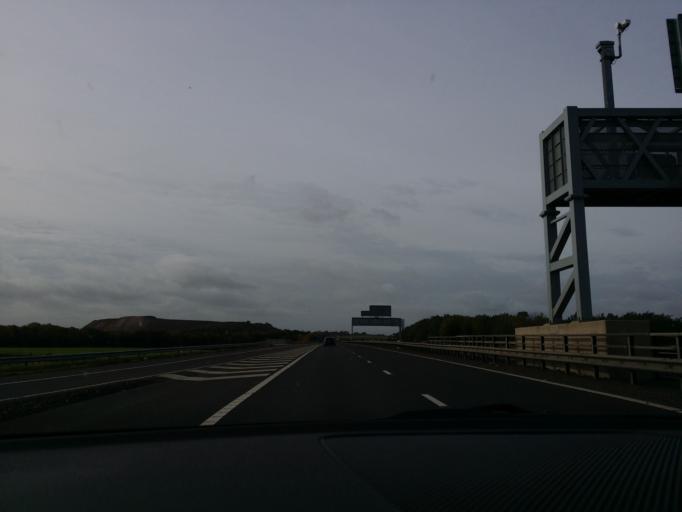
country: GB
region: Scotland
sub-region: Edinburgh
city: Kirkliston
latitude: 55.9562
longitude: -3.4238
